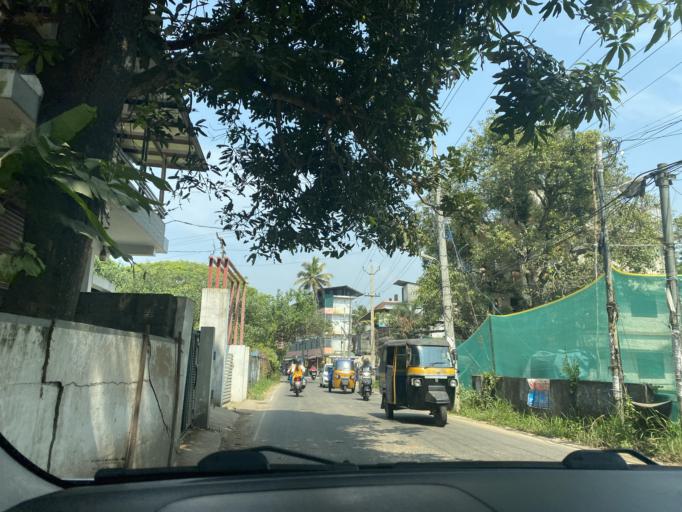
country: IN
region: Kerala
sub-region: Alappuzha
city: Arukutti
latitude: 9.9079
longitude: 76.3192
